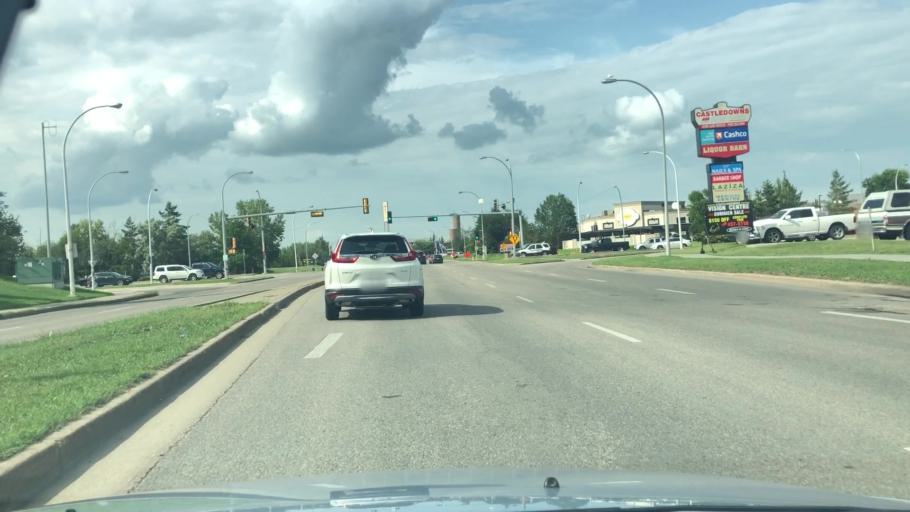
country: CA
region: Alberta
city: Edmonton
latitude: 53.6133
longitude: -113.5167
